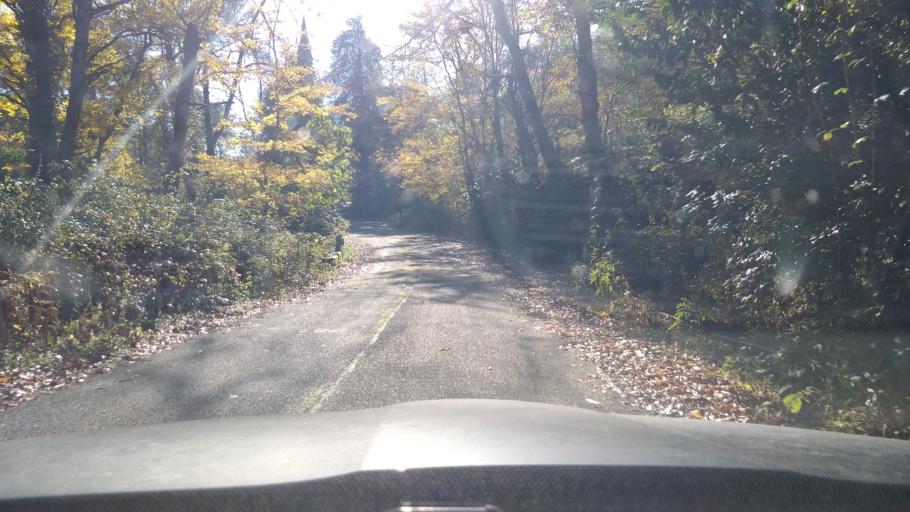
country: GE
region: Abkhazia
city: Bich'vinta
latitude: 43.1856
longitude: 40.4538
